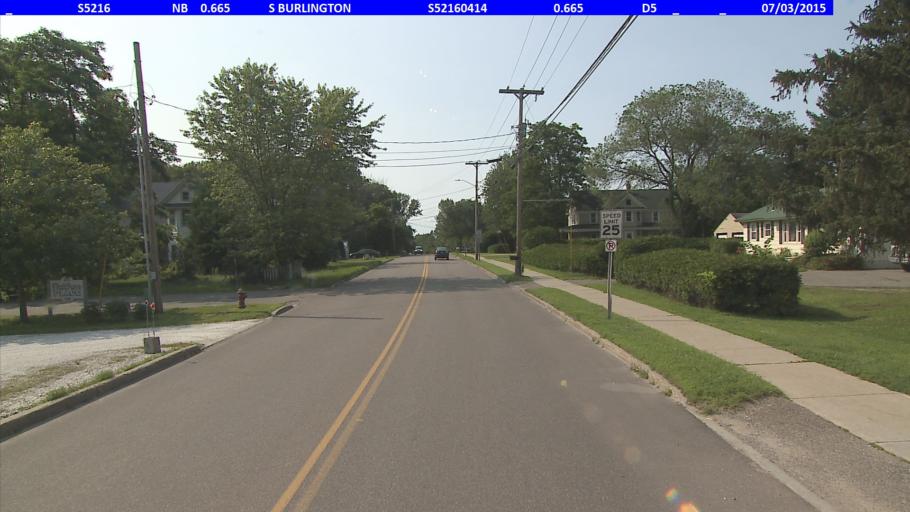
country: US
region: Vermont
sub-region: Chittenden County
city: South Burlington
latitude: 44.4762
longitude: -73.1739
